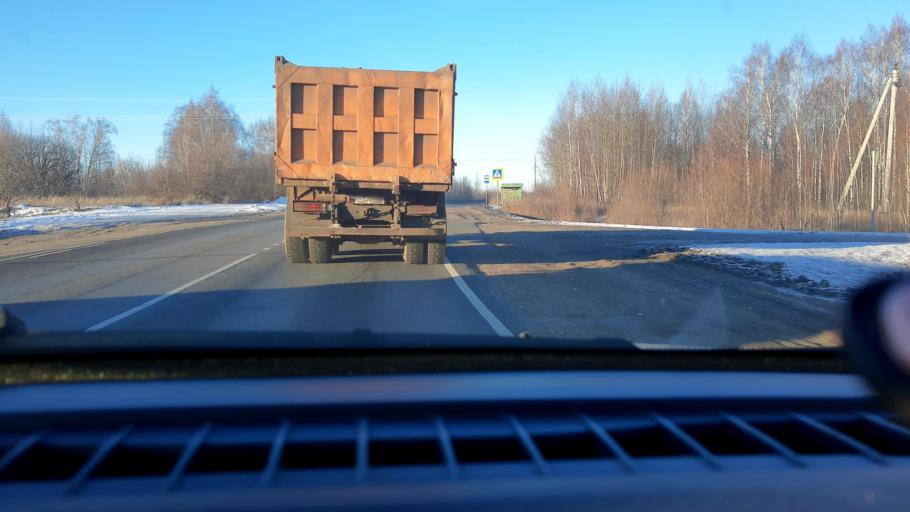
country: RU
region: Nizjnij Novgorod
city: Kstovo
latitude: 56.0511
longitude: 44.1424
